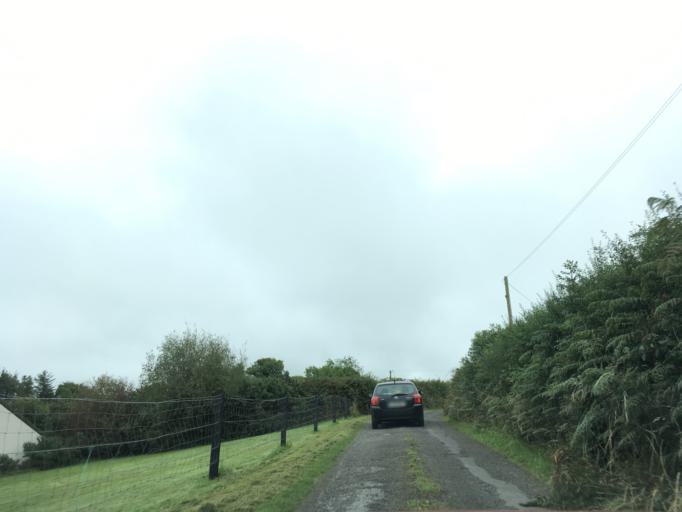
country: IE
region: Munster
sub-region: An Clar
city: Ennis
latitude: 52.7288
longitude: -9.0894
